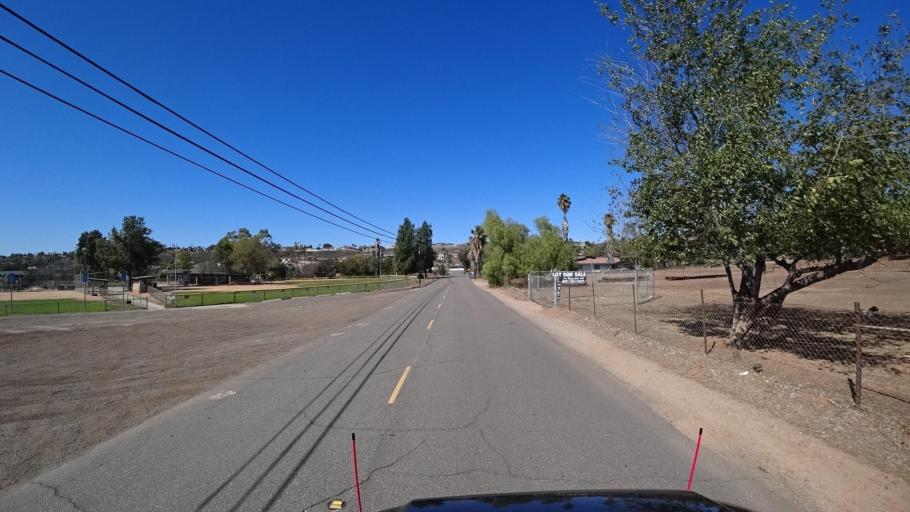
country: US
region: California
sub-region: San Diego County
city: Harbison Canyon
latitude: 32.8572
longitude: -116.8583
